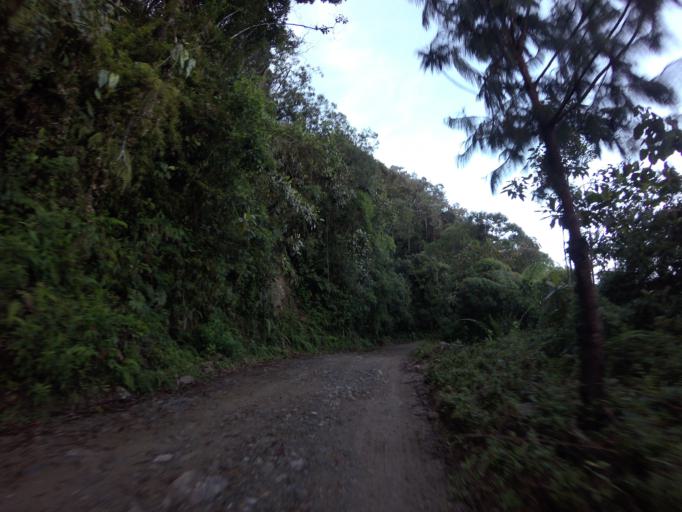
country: CO
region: Caldas
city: Pensilvania
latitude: 5.4147
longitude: -75.1317
